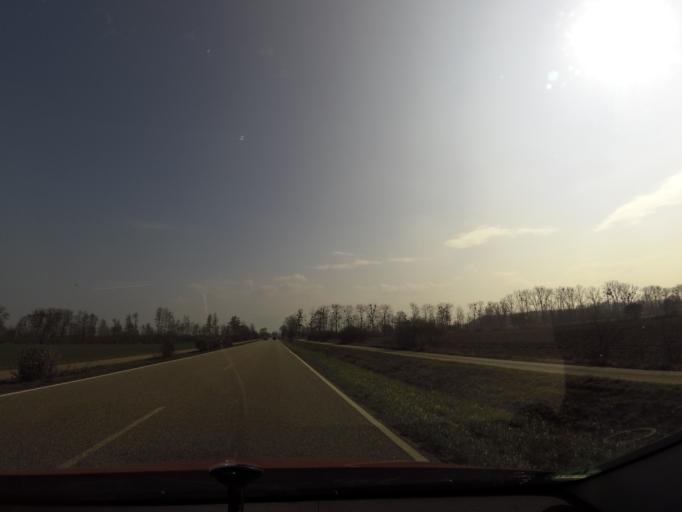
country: DE
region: Baden-Wuerttemberg
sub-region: Freiburg Region
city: Renchen
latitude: 48.6477
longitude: 7.9998
